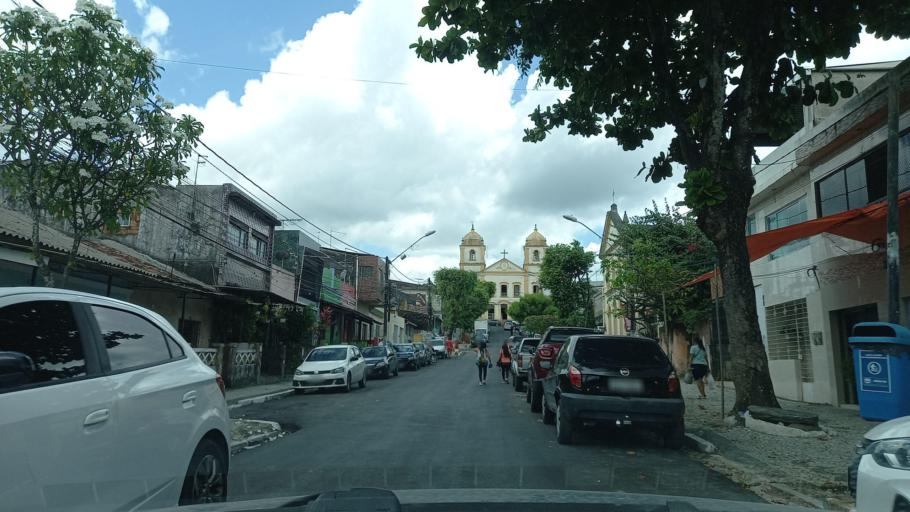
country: BR
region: Pernambuco
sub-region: Jaboatao Dos Guararapes
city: Jaboatao dos Guararapes
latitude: -8.1111
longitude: -35.0194
